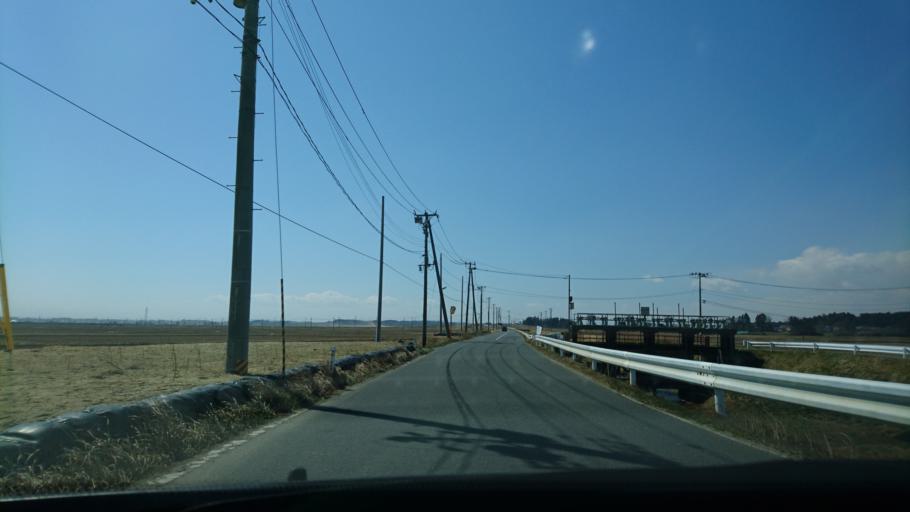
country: JP
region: Iwate
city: Ichinoseki
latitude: 38.7546
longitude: 141.1347
